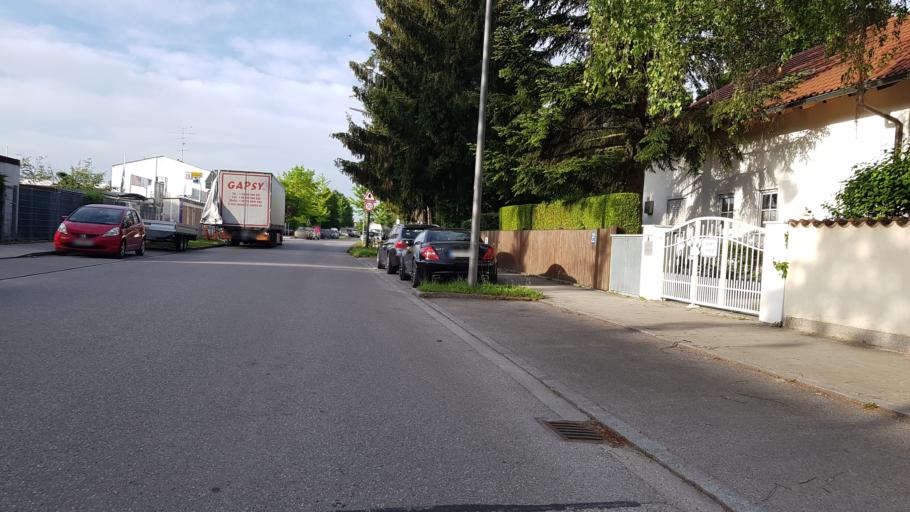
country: DE
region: Bavaria
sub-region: Upper Bavaria
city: Unterhaching
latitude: 48.0905
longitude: 11.6305
